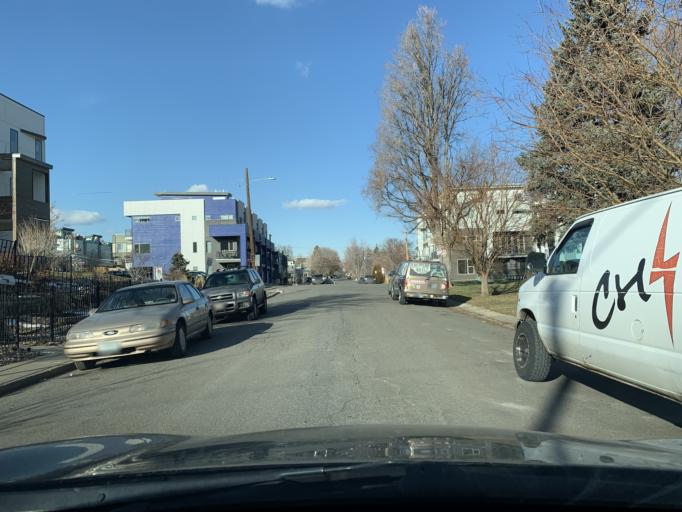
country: US
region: Colorado
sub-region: Jefferson County
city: Edgewater
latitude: 39.7459
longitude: -105.0284
